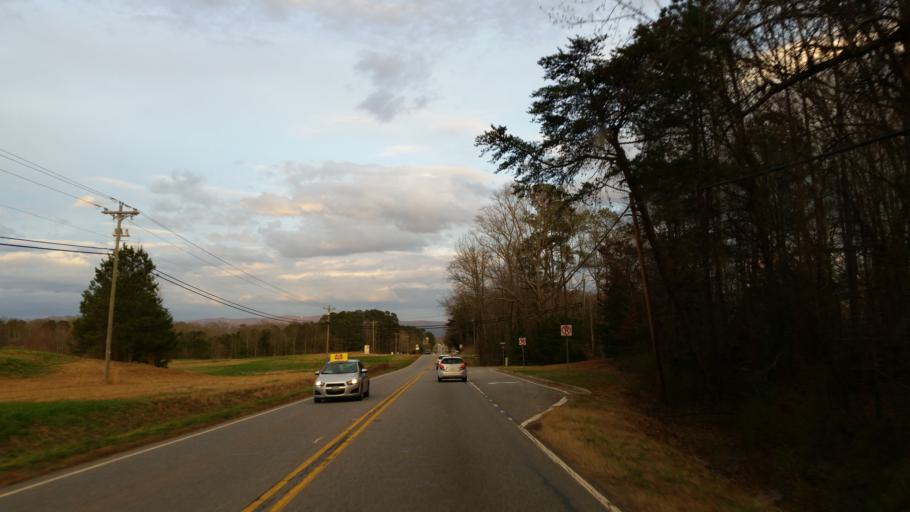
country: US
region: Georgia
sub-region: Pickens County
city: Jasper
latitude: 34.4646
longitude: -84.4738
